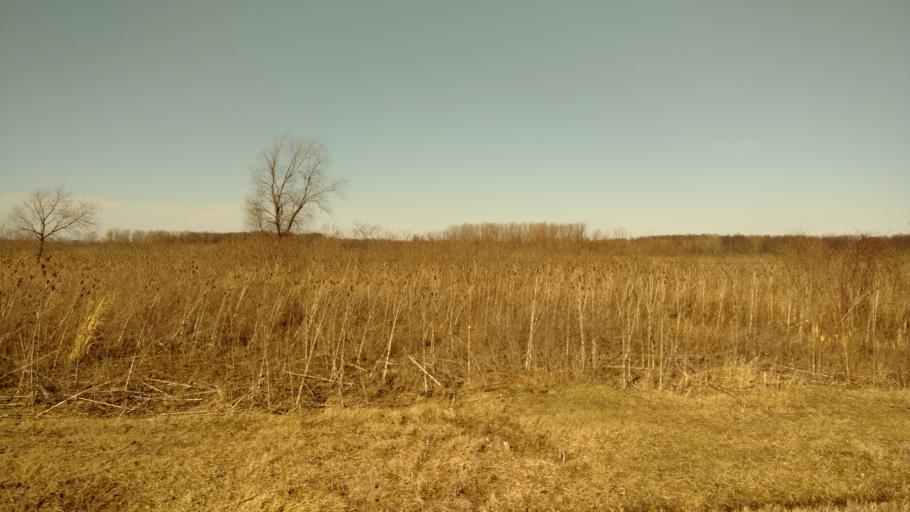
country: US
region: Ohio
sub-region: Wyandot County
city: Upper Sandusky
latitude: 40.7022
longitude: -83.2716
